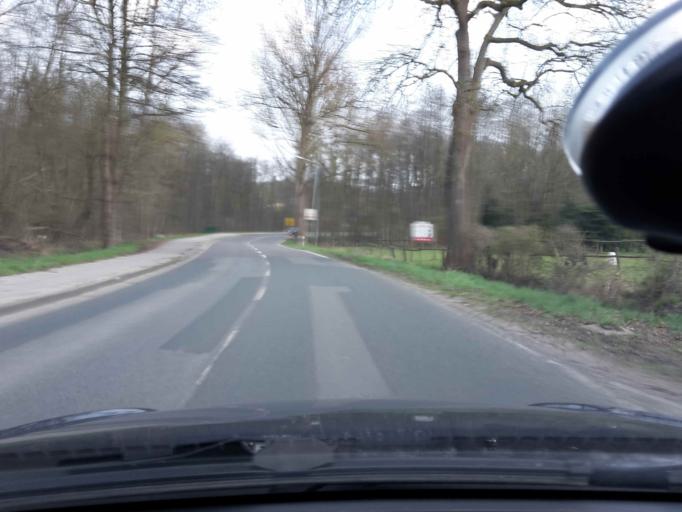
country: DE
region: Lower Saxony
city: Buchholz in der Nordheide
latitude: 53.3021
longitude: 9.8770
